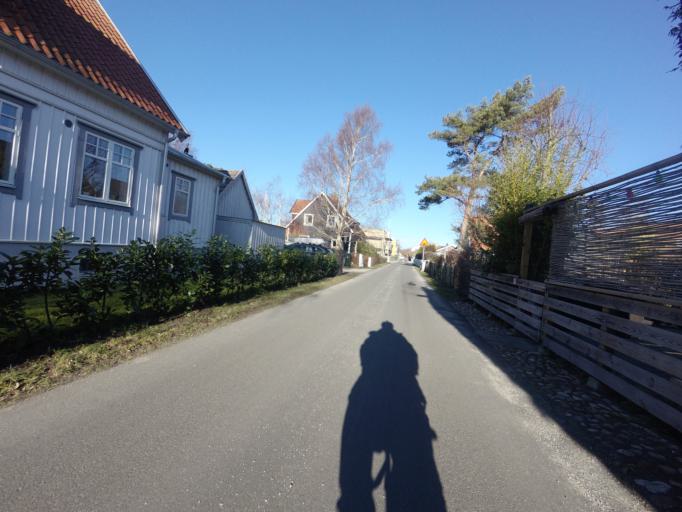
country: SE
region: Skane
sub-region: Vellinge Kommun
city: Hollviken
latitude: 55.4184
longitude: 12.9558
